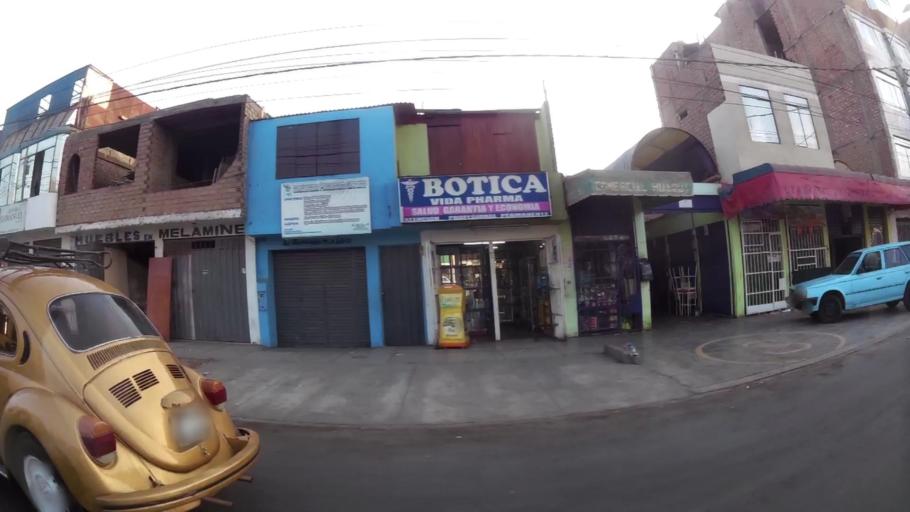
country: PE
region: Callao
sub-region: Callao
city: Callao
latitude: -11.9971
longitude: -77.1084
